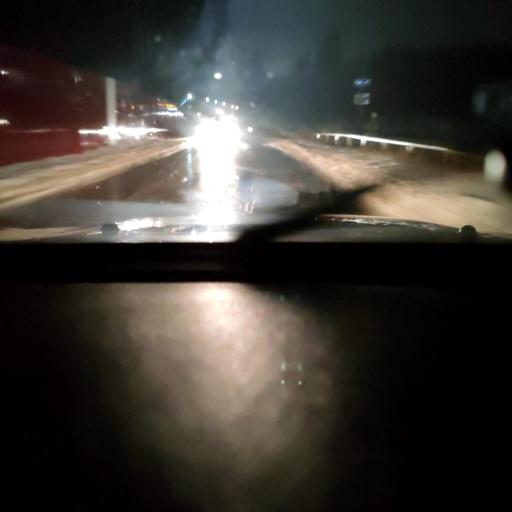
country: RU
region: Voronezj
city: Podgornoye
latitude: 51.7849
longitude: 39.1467
